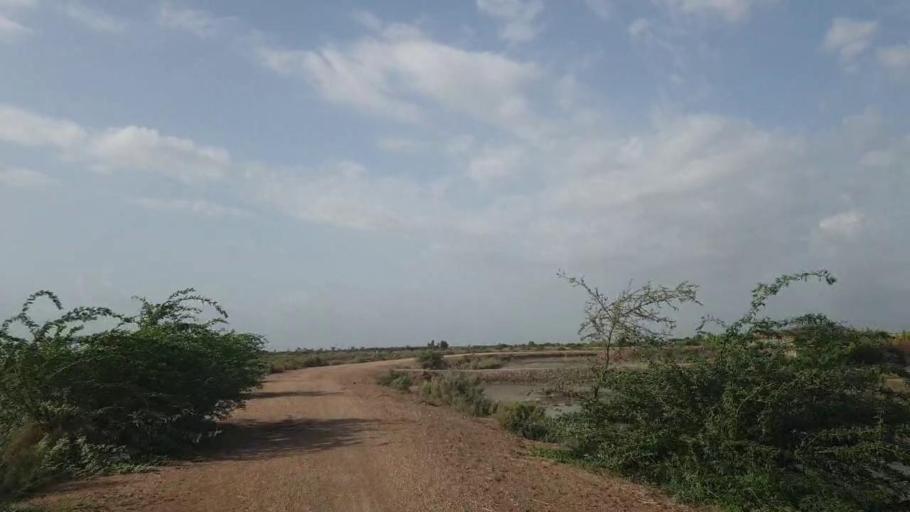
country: PK
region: Sindh
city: Kadhan
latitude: 24.6320
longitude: 69.0875
